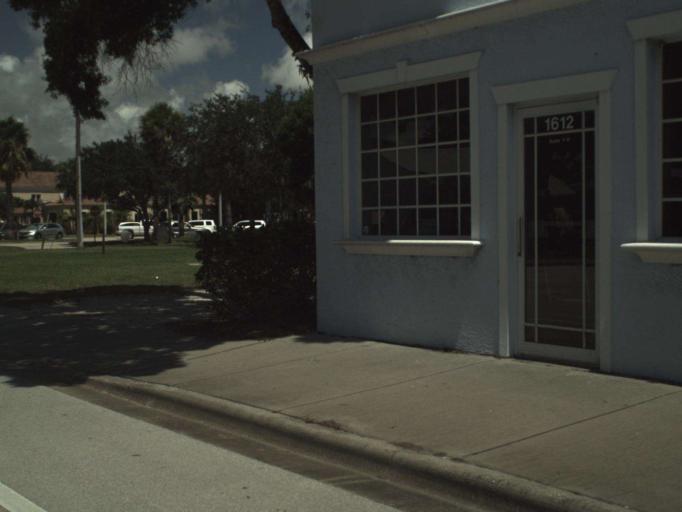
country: US
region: Florida
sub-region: Indian River County
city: Vero Beach
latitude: 27.6387
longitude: -80.4018
